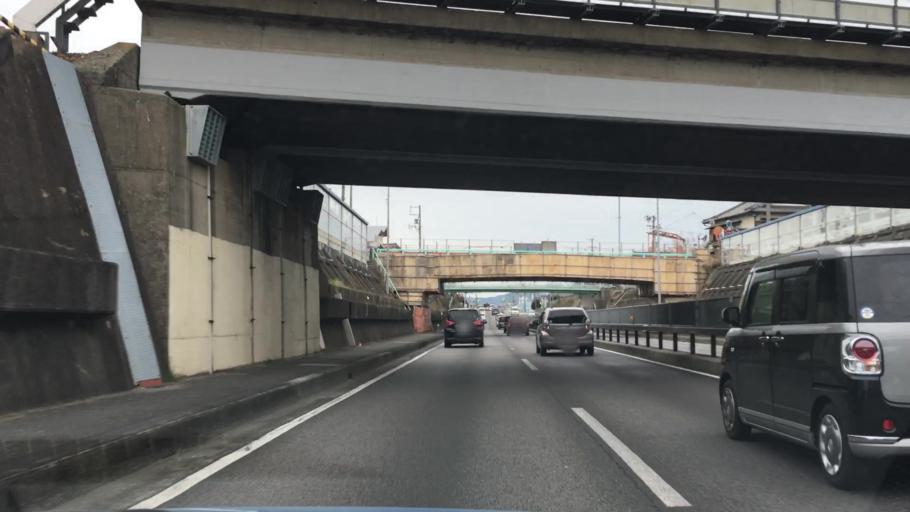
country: JP
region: Aichi
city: Kozakai-cho
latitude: 34.7995
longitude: 137.3651
